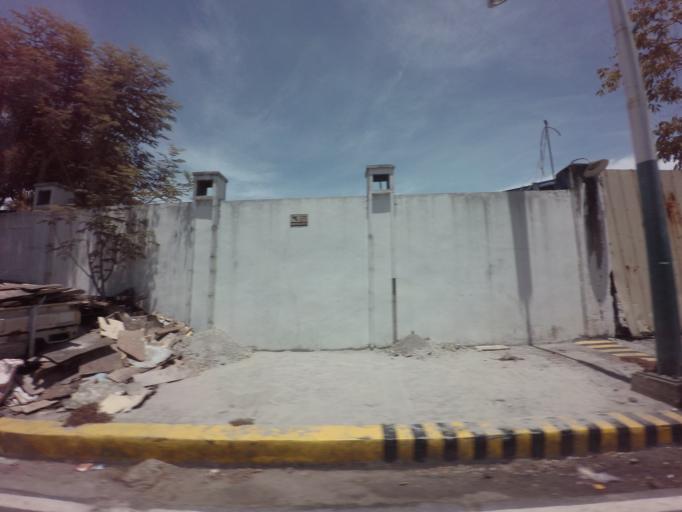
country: PH
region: Metro Manila
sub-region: Makati City
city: Makati City
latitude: 14.5059
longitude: 121.0276
